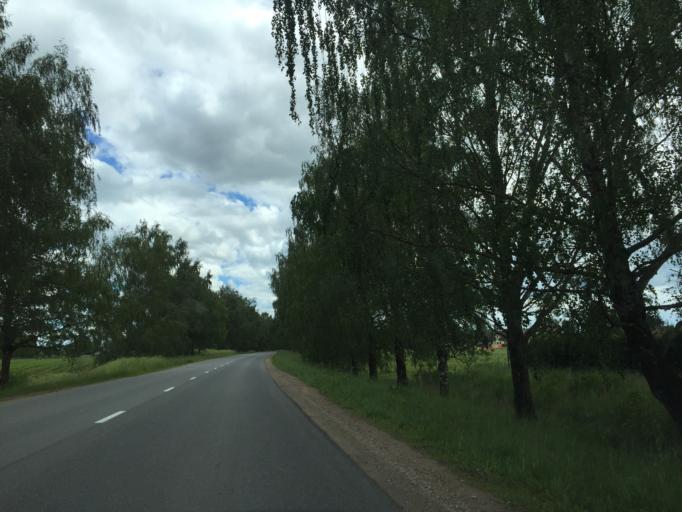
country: LV
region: Lecava
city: Iecava
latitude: 56.6038
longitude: 24.2142
